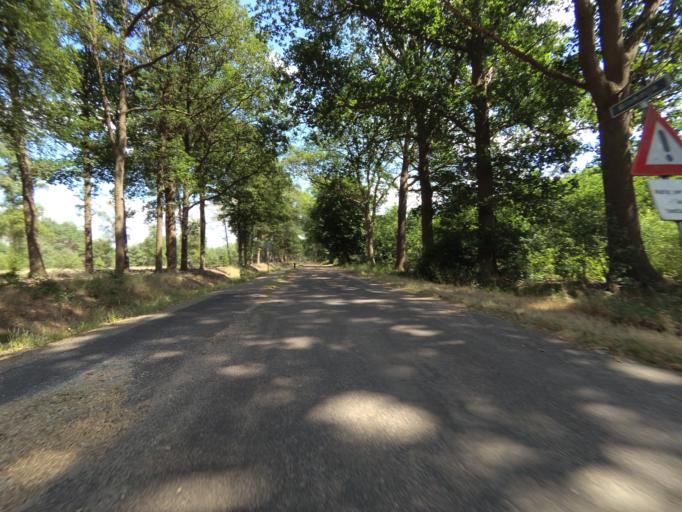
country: NL
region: Overijssel
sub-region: Gemeente Wierden
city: Wierden
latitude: 52.3491
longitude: 6.5100
